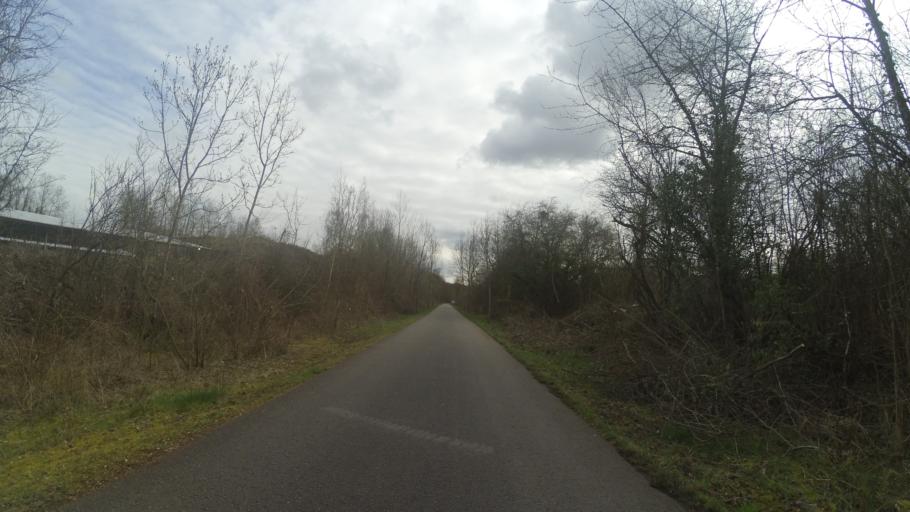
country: DE
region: Saarland
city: Gersheim
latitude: 49.1534
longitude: 7.2079
